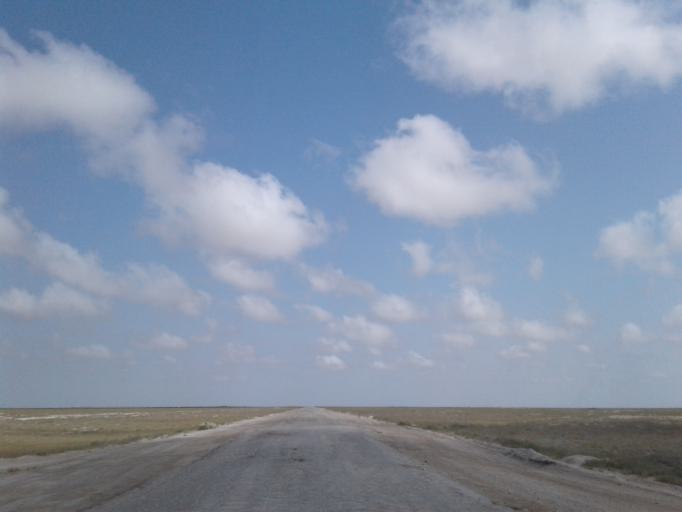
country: IR
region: Golestan
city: Gomishan
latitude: 37.6055
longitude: 53.9250
